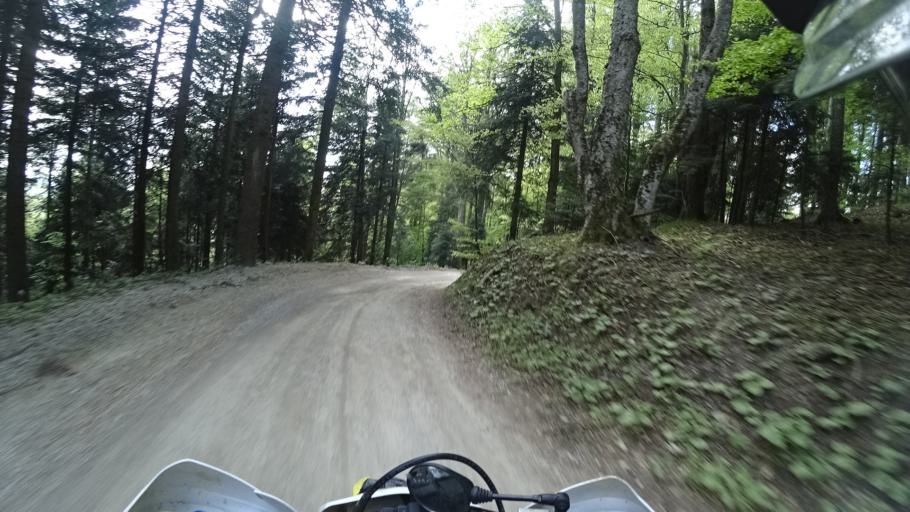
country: HR
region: Grad Zagreb
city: Kasina
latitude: 45.9087
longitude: 15.9439
